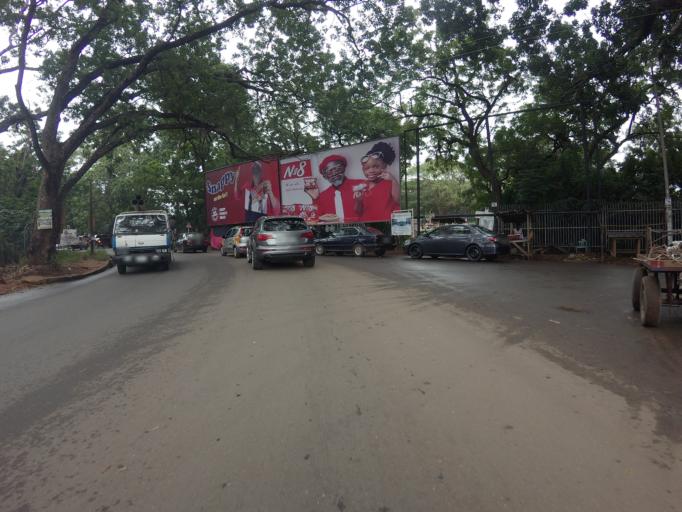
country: GH
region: Greater Accra
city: Dome
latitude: 5.6290
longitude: -0.2203
